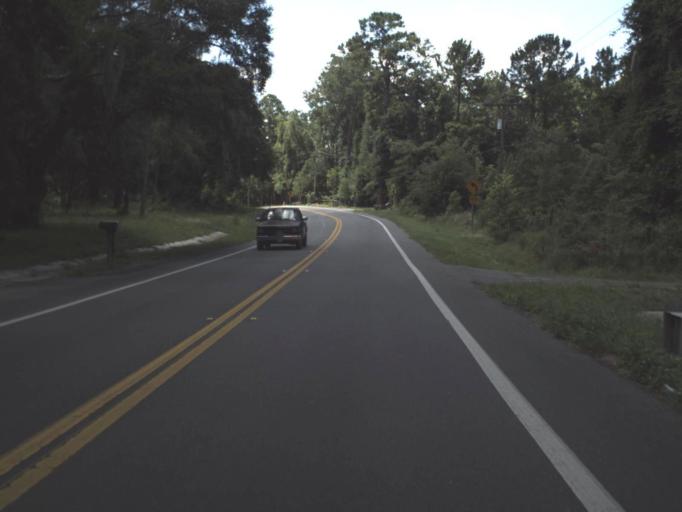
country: US
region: Florida
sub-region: Clay County
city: Keystone Heights
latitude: 29.6920
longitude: -82.0399
